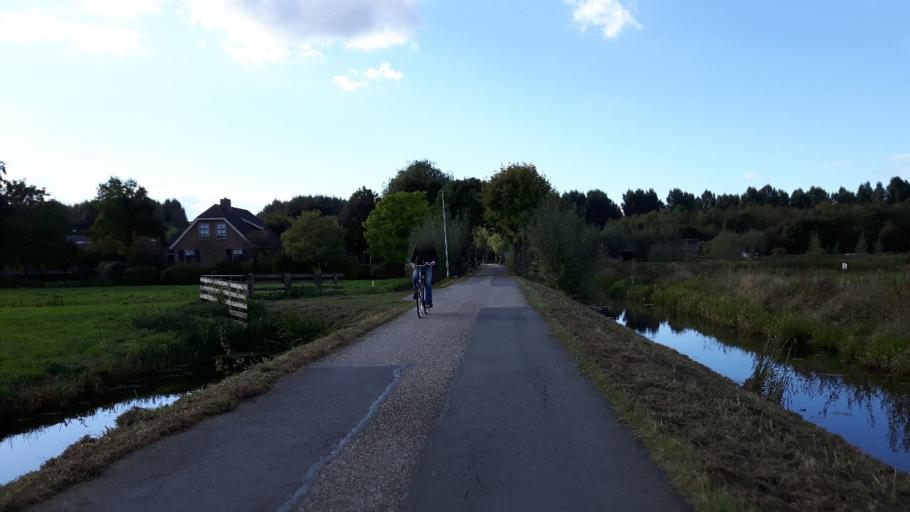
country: NL
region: Utrecht
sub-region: Gemeente Vianen
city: Vianen
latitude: 51.9679
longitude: 5.0802
